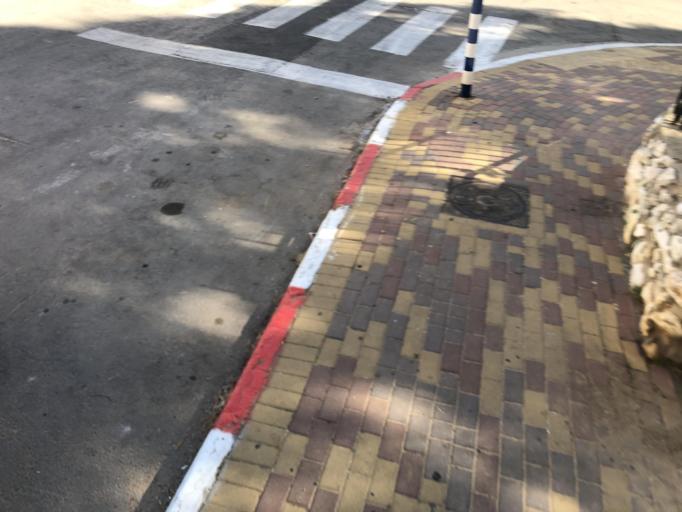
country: IL
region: Central District
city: Yehud
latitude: 32.0340
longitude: 34.8917
